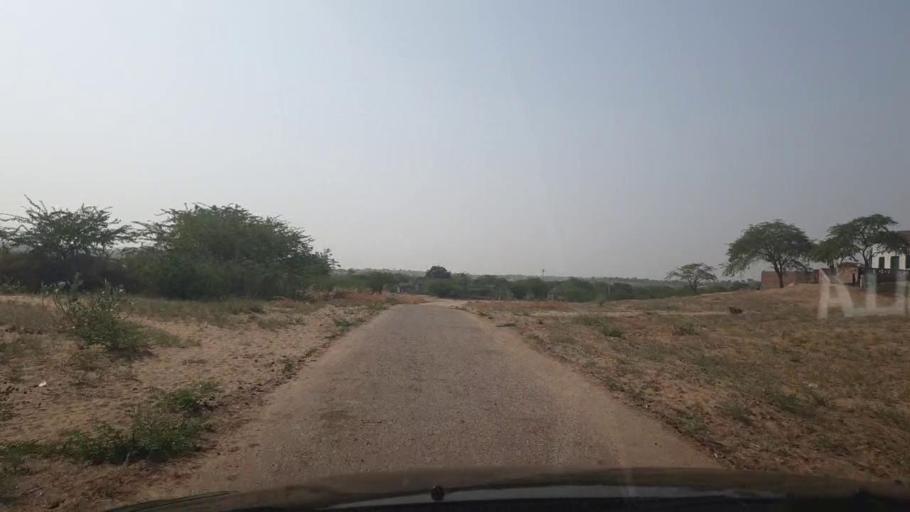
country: PK
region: Sindh
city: Islamkot
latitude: 25.0100
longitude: 70.2117
